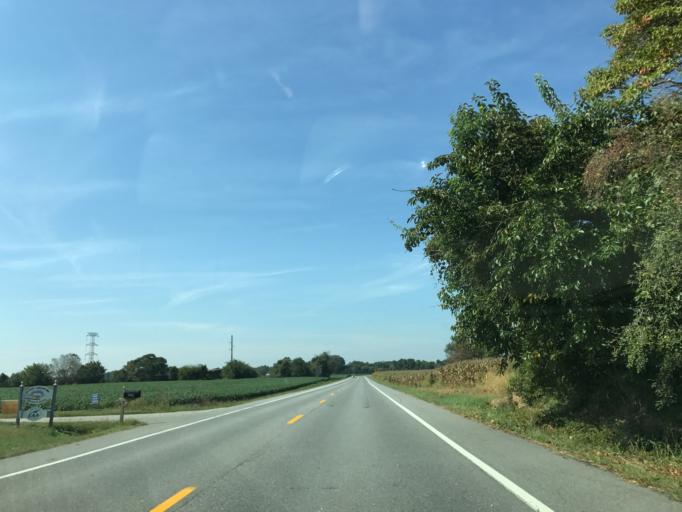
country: US
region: Delaware
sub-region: New Castle County
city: Townsend
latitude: 39.3038
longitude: -75.8011
